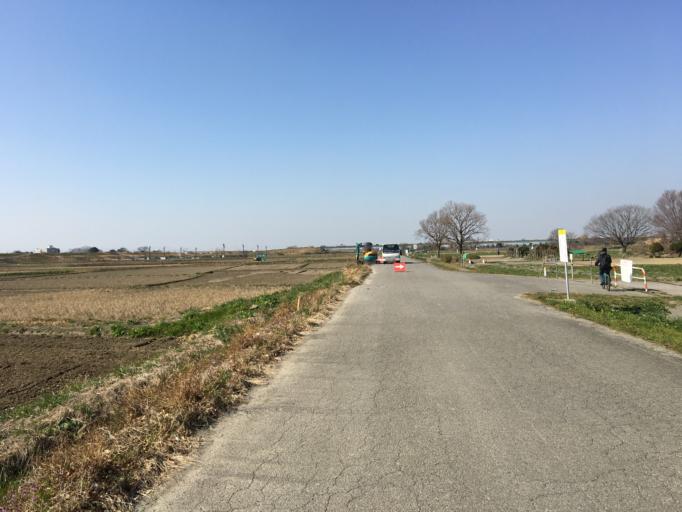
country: JP
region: Saitama
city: Shiki
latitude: 35.8482
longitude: 139.5948
